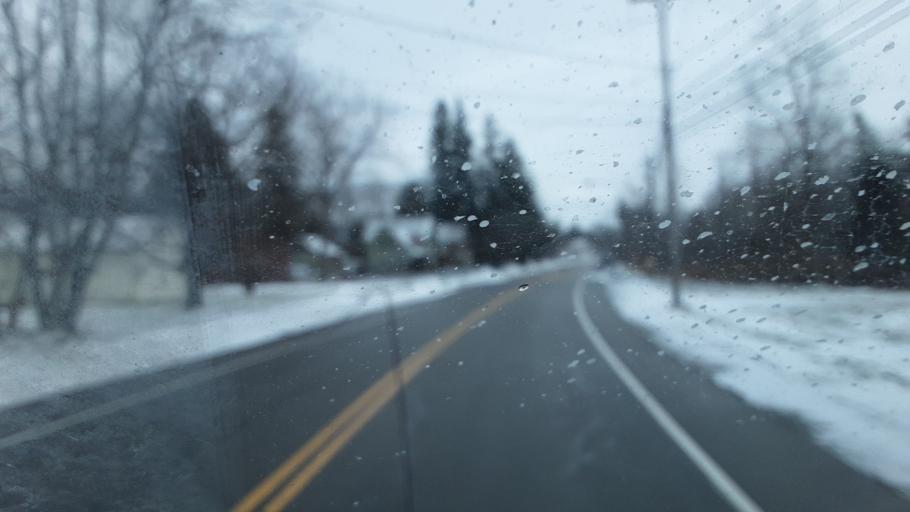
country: US
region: New York
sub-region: Allegany County
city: Belmont
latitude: 42.2244
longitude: -78.0274
